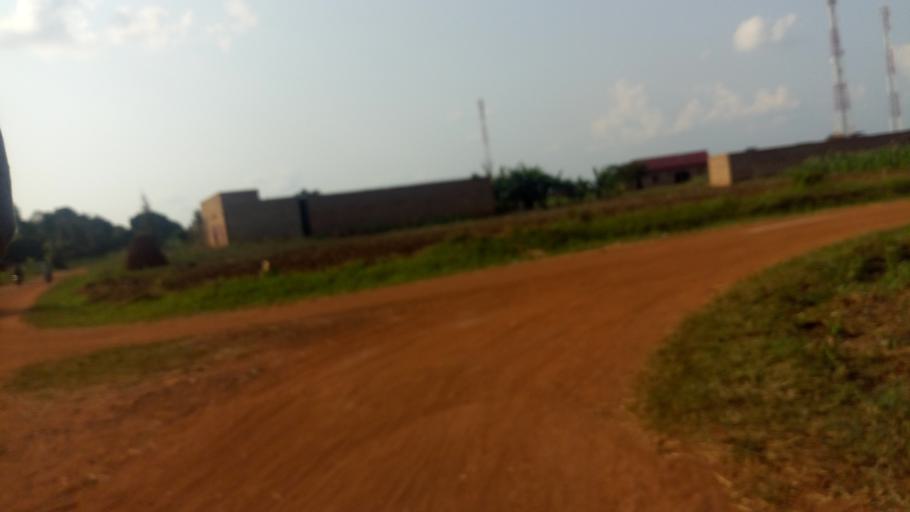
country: UG
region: Western Region
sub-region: Kiryandongo District
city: Kiryandongo
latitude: 1.8054
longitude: 32.0081
